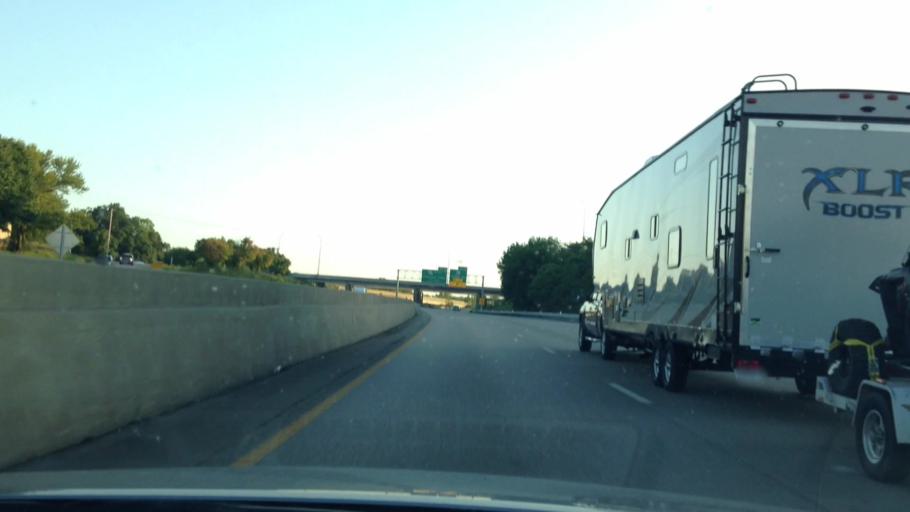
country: US
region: Missouri
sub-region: Clay County
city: Claycomo
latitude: 39.1905
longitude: -94.5146
